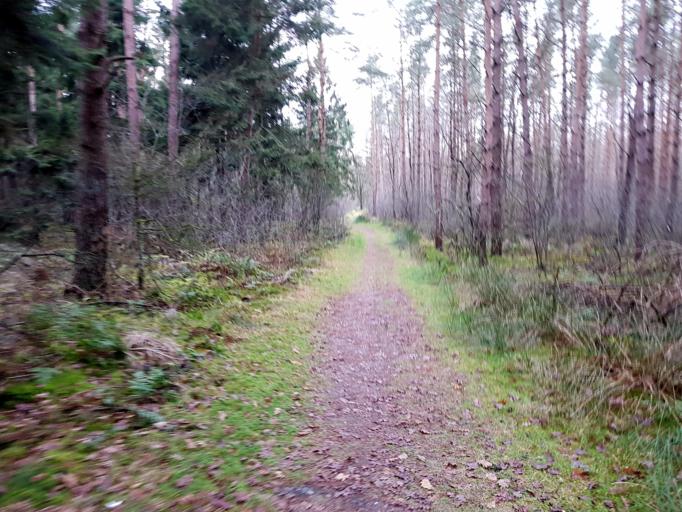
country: NL
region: Utrecht
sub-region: Gemeente Utrechtse Heuvelrug
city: Maarsbergen
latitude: 52.0395
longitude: 5.3946
